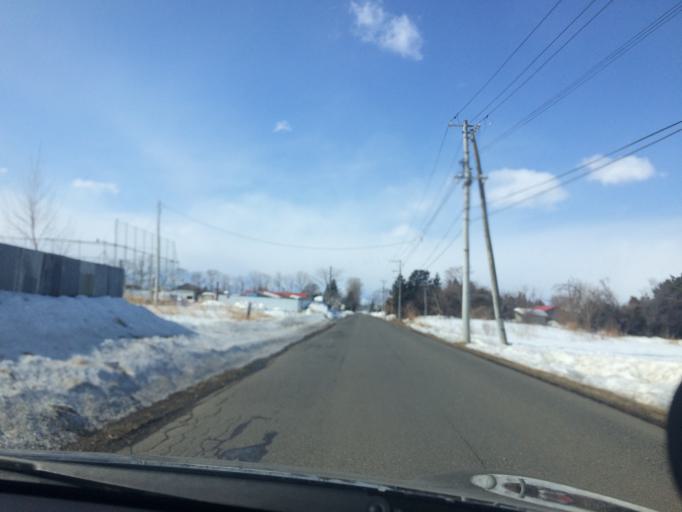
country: JP
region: Hokkaido
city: Obihiro
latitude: 42.9202
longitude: 143.1089
